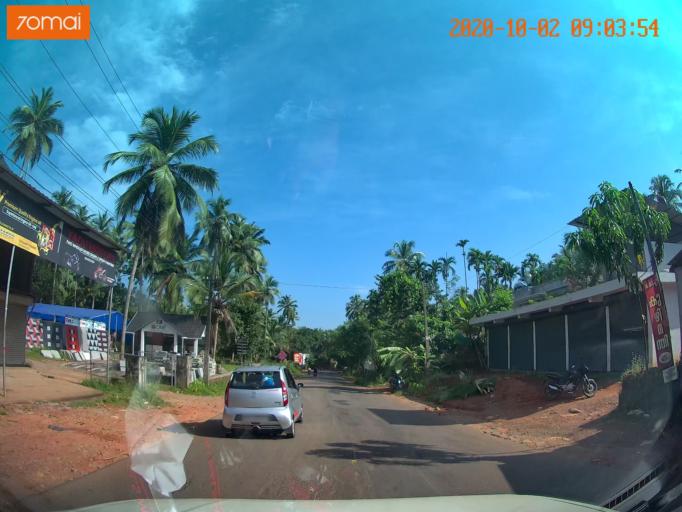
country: IN
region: Kerala
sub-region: Kozhikode
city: Naduvannur
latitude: 11.4731
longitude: 75.7743
